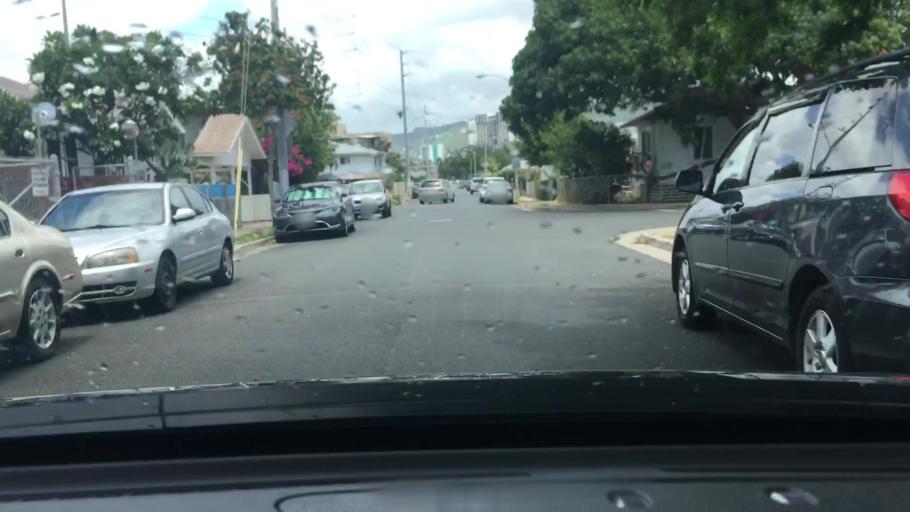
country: US
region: Hawaii
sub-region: Honolulu County
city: Honolulu
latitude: 21.2735
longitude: -157.8142
